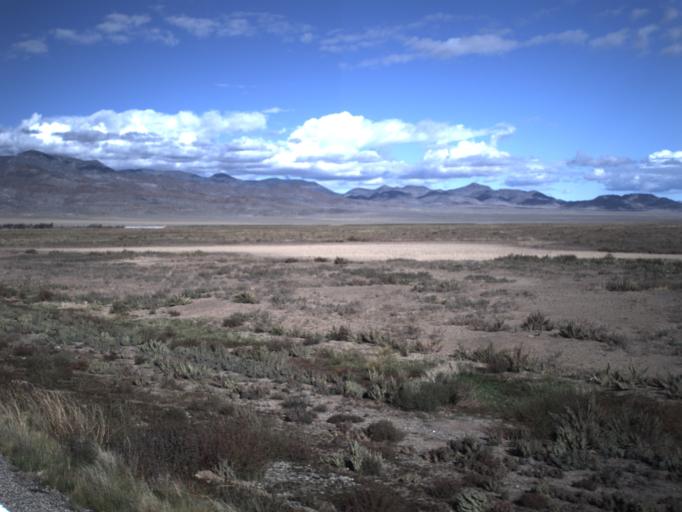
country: US
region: Utah
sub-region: Beaver County
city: Milford
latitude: 38.4689
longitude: -113.4022
